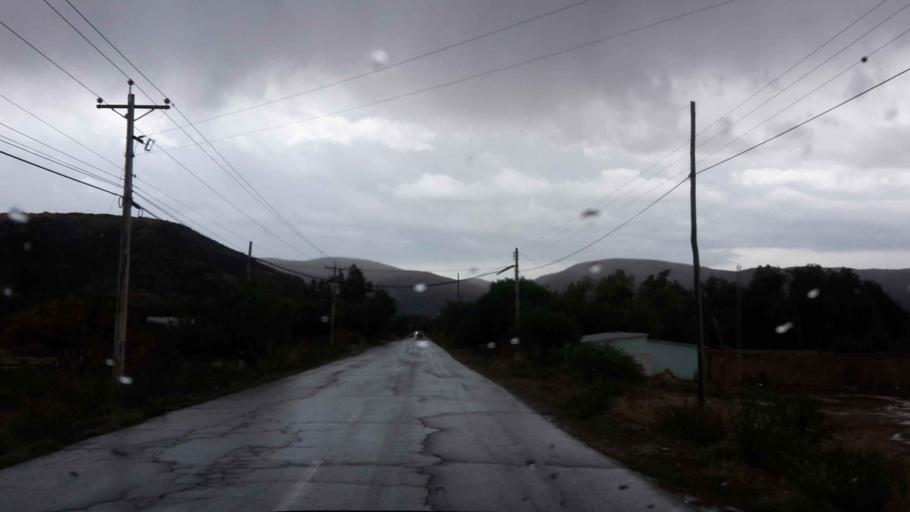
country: BO
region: Cochabamba
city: Tarata
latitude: -17.5506
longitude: -66.0958
